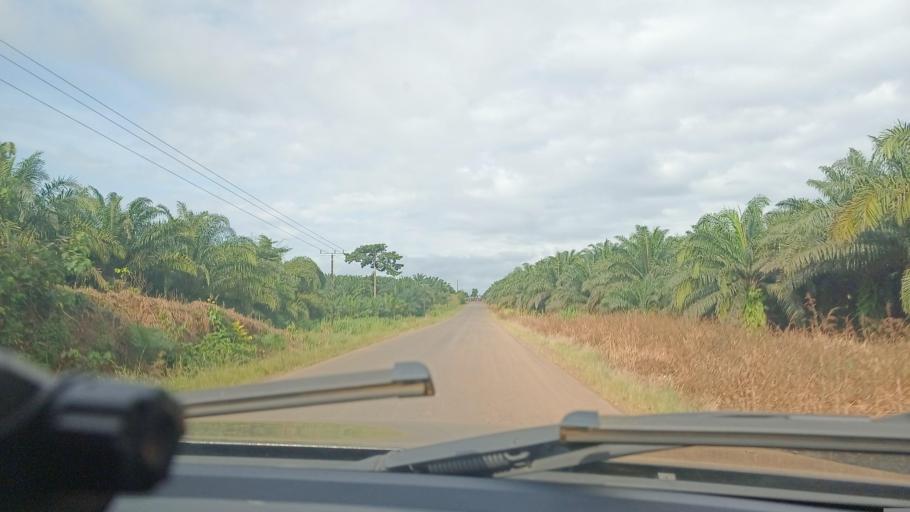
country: LR
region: Bomi
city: Tubmanburg
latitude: 6.7124
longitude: -10.9627
